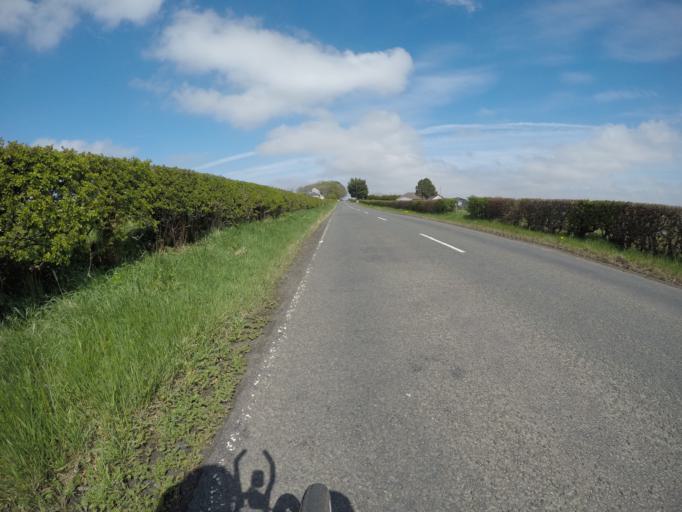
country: GB
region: Scotland
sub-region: East Ayrshire
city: Stewarton
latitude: 55.6971
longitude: -4.4873
